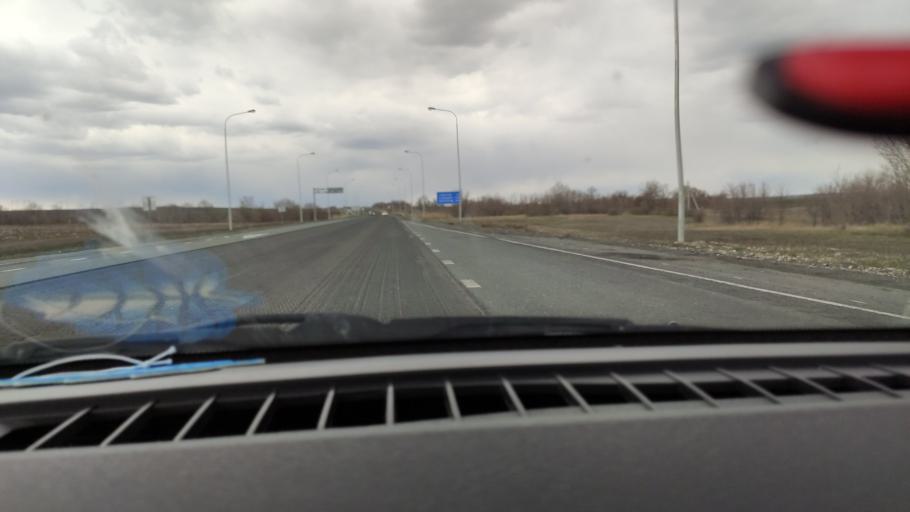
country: RU
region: Saratov
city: Yelshanka
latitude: 51.7940
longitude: 46.1623
